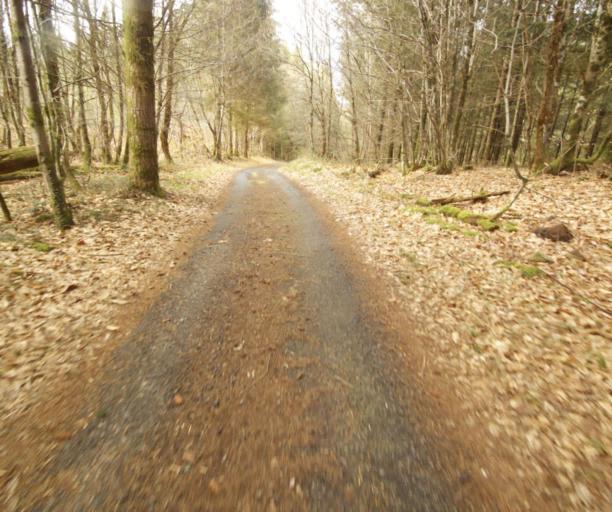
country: FR
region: Limousin
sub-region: Departement de la Correze
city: Saint-Privat
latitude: 45.2205
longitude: 1.9973
